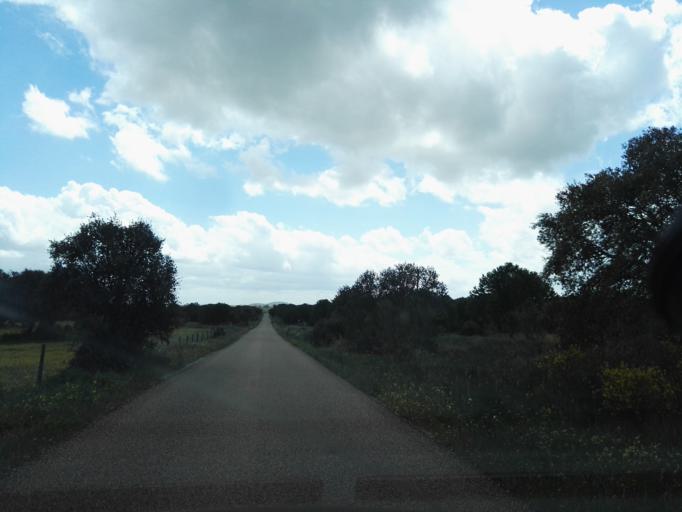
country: PT
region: Portalegre
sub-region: Elvas
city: Elvas
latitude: 38.9833
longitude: -7.1765
